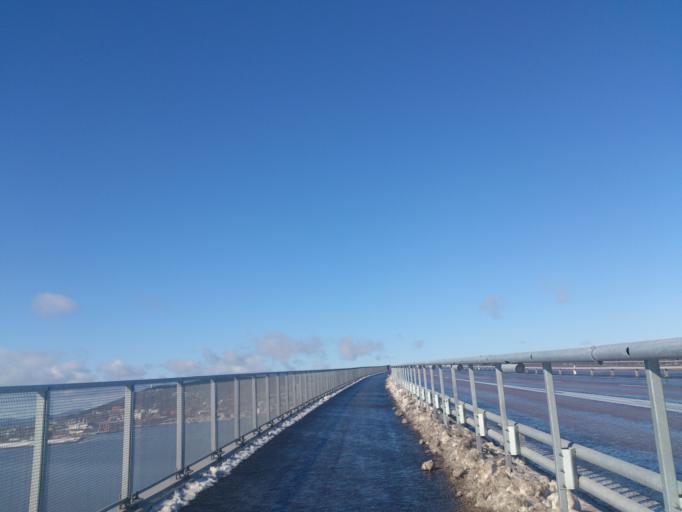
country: SE
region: Vaesternorrland
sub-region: Sundsvalls Kommun
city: Sundsvall
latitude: 62.3835
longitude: 17.3482
